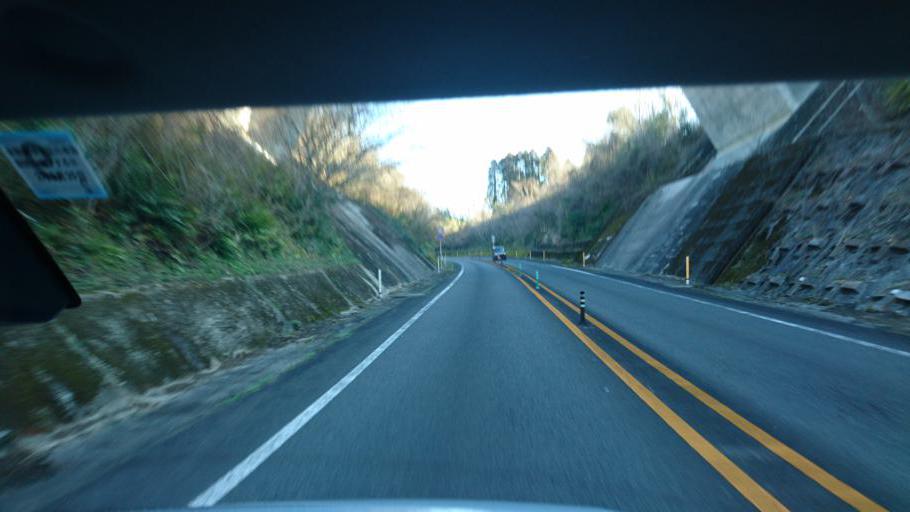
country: JP
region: Miyazaki
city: Miyazaki-shi
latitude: 31.8606
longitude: 131.3668
